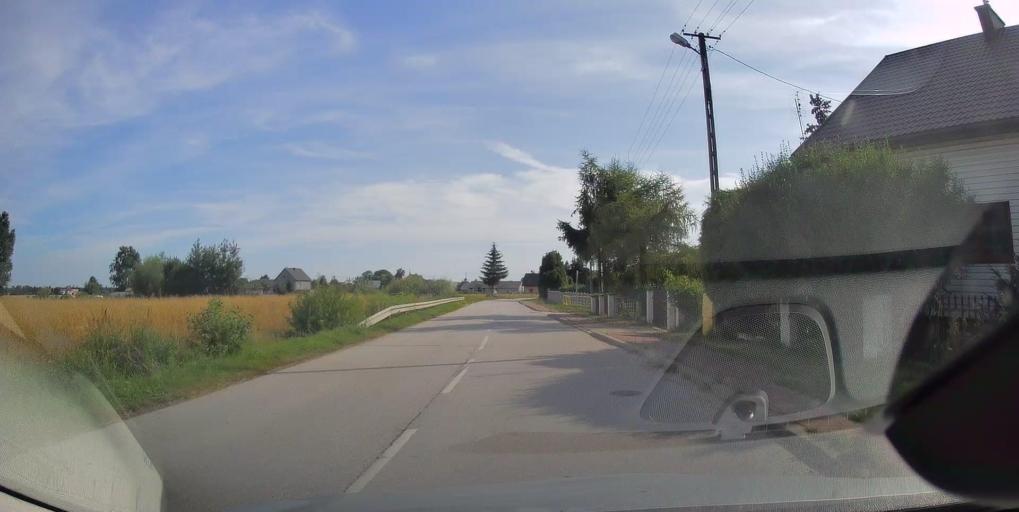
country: PL
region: Lodz Voivodeship
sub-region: Powiat opoczynski
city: Mniszkow
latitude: 51.3353
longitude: 20.0317
